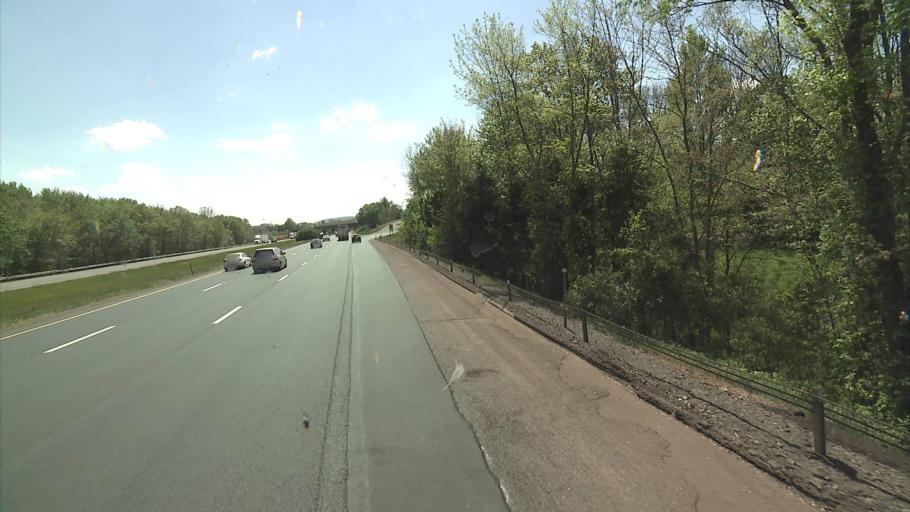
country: US
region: Connecticut
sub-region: Hartford County
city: Plainville
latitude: 41.6158
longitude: -72.8965
